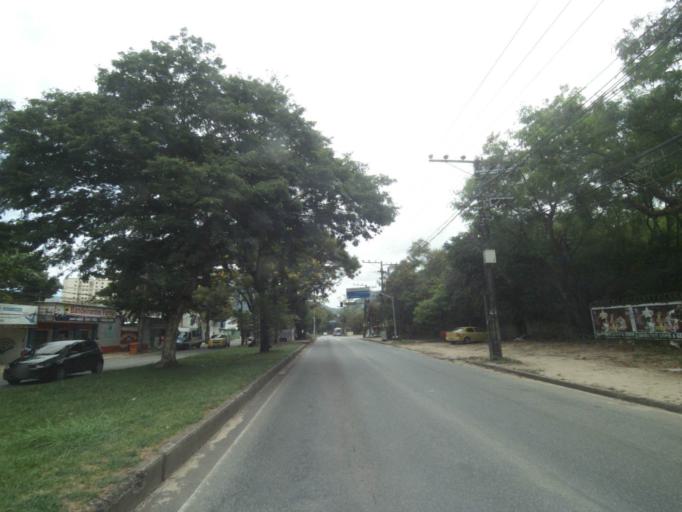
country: BR
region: Rio de Janeiro
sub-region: Nilopolis
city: Nilopolis
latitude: -22.9631
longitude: -43.4026
